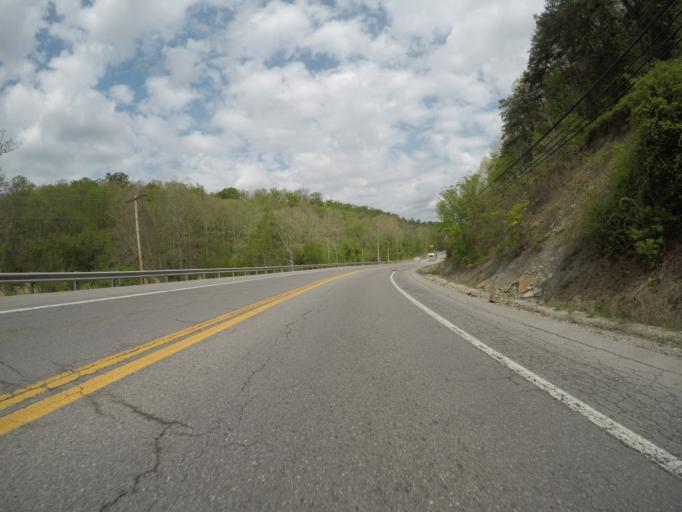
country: US
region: West Virginia
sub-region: Kanawha County
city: South Charleston
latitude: 38.3448
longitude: -81.7099
